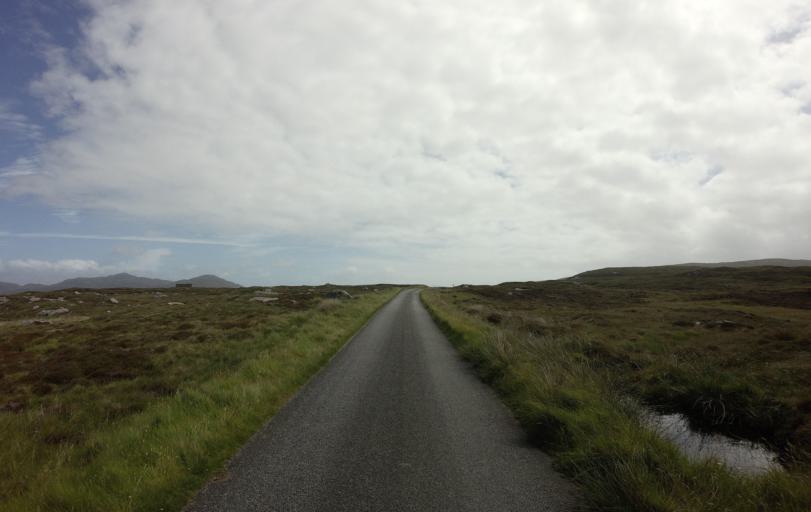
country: GB
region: Scotland
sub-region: Eilean Siar
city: Isle of South Uist
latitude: 57.1380
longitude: -7.3516
